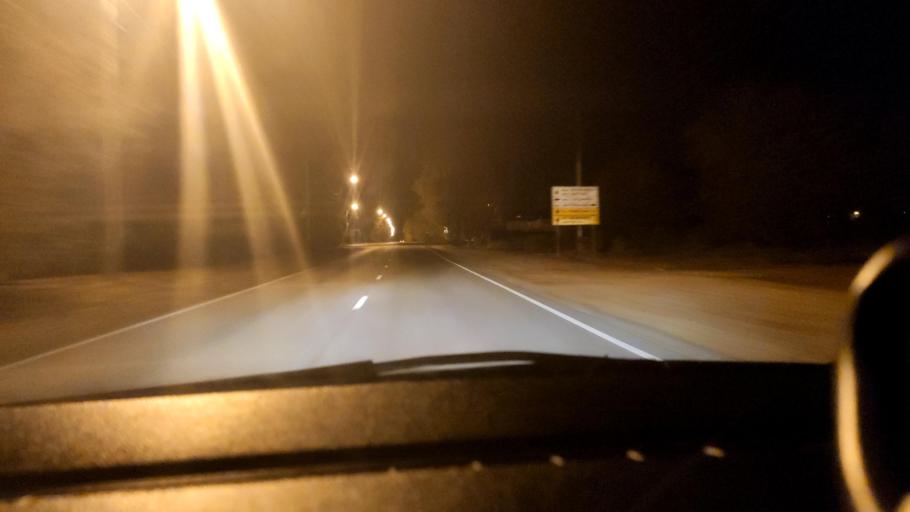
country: RU
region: Voronezj
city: Pridonskoy
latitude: 51.6429
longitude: 39.0938
